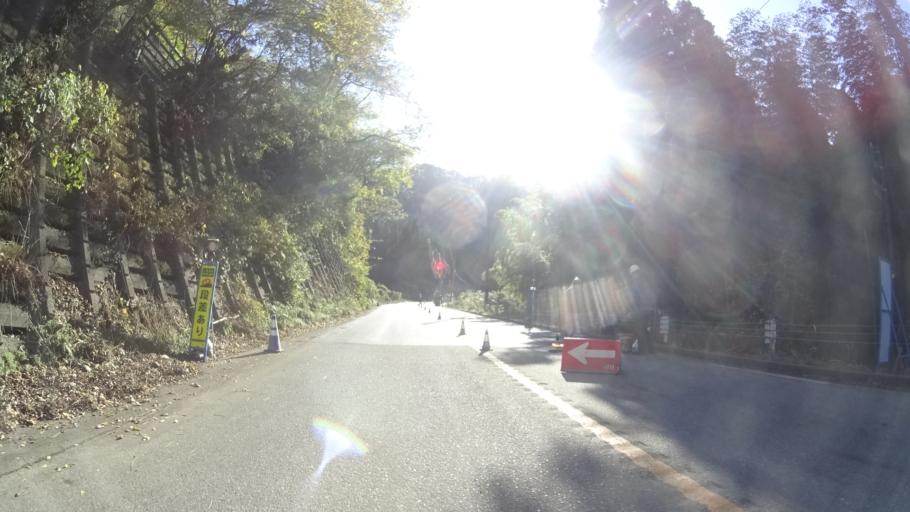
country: JP
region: Ishikawa
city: Tsurugi-asahimachi
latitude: 36.3718
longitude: 136.5817
